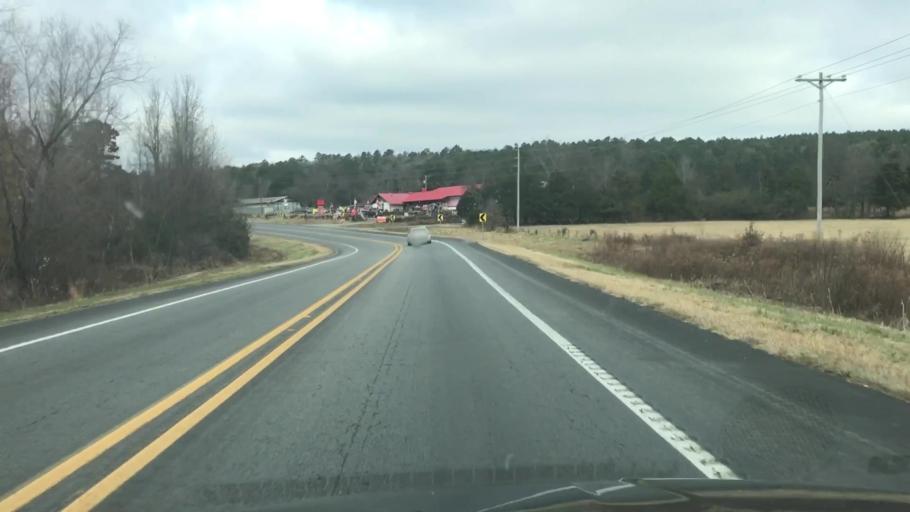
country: US
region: Arkansas
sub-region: Scott County
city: Waldron
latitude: 34.8363
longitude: -94.0451
